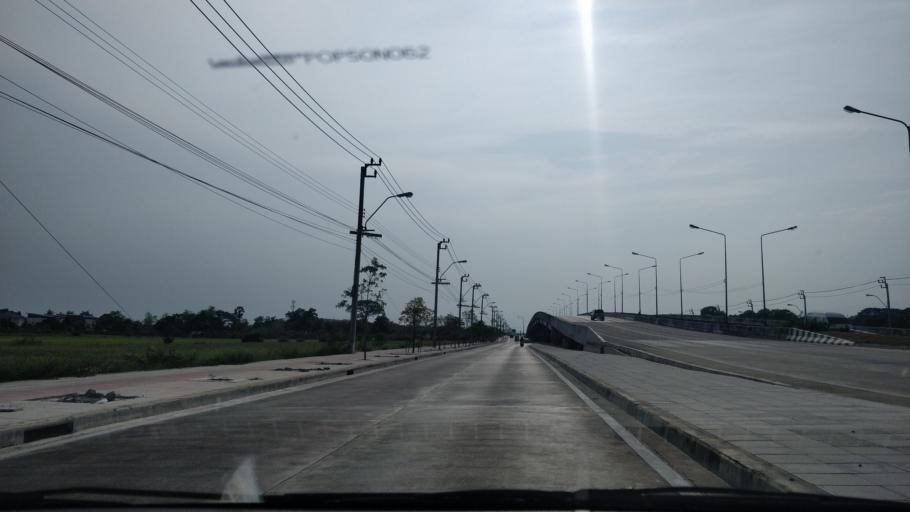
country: TH
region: Bangkok
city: Saphan Sung
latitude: 13.7547
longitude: 100.7273
